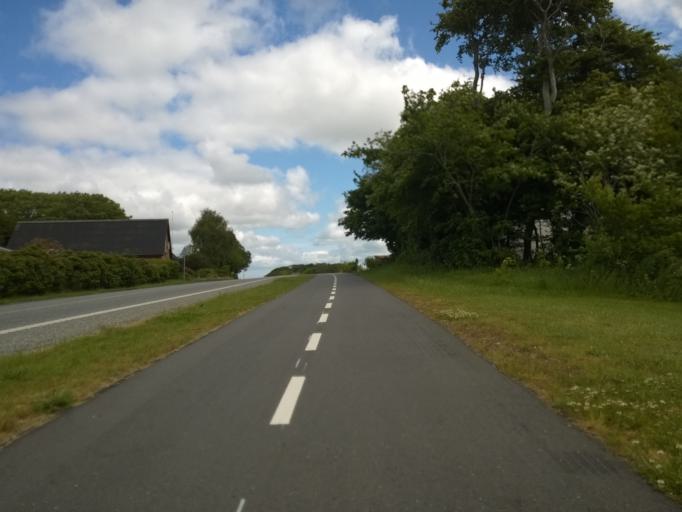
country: DK
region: Central Jutland
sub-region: Holstebro Kommune
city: Vinderup
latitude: 56.4760
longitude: 8.7973
